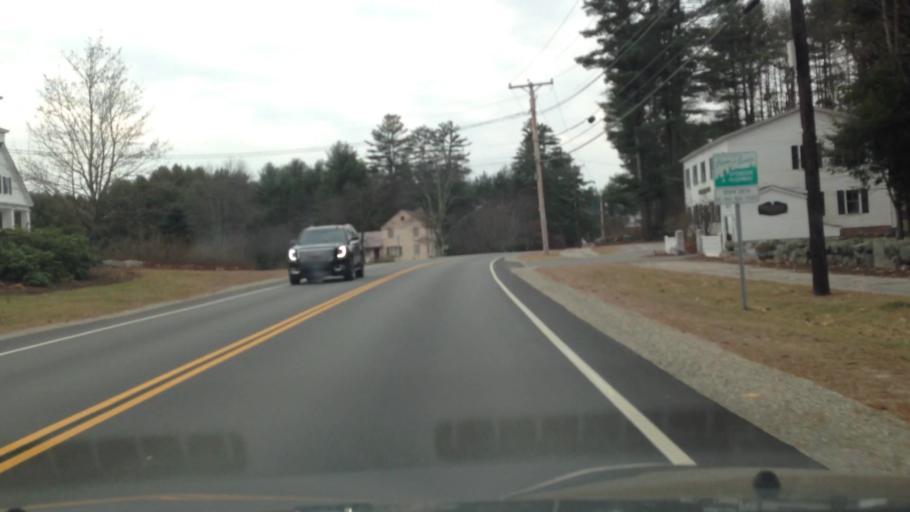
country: US
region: New Hampshire
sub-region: Cheshire County
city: Swanzey
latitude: 42.8731
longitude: -72.2815
